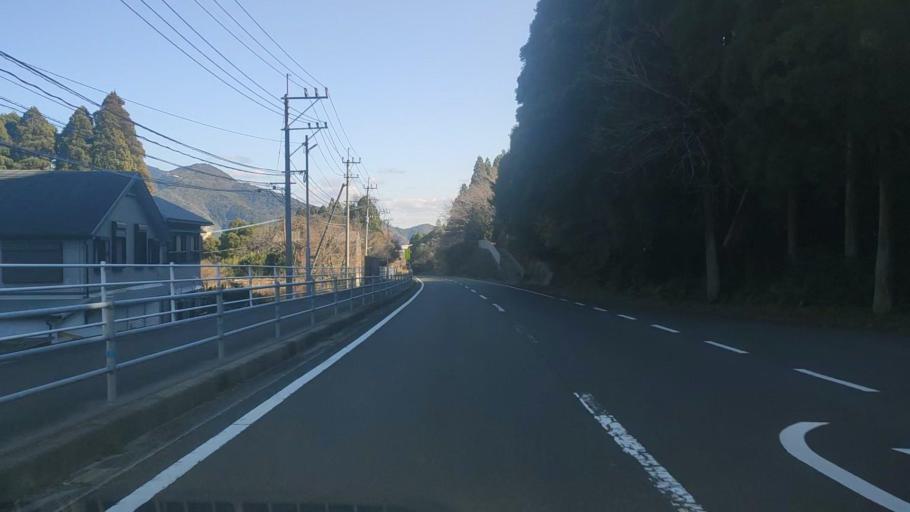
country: JP
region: Oita
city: Saiki
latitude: 32.8006
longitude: 131.9386
